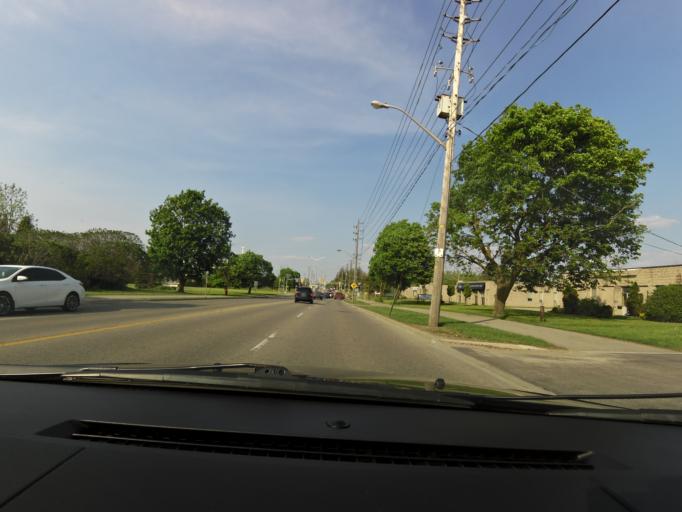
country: CA
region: Ontario
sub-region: Wellington County
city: Guelph
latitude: 43.5597
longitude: -80.2847
